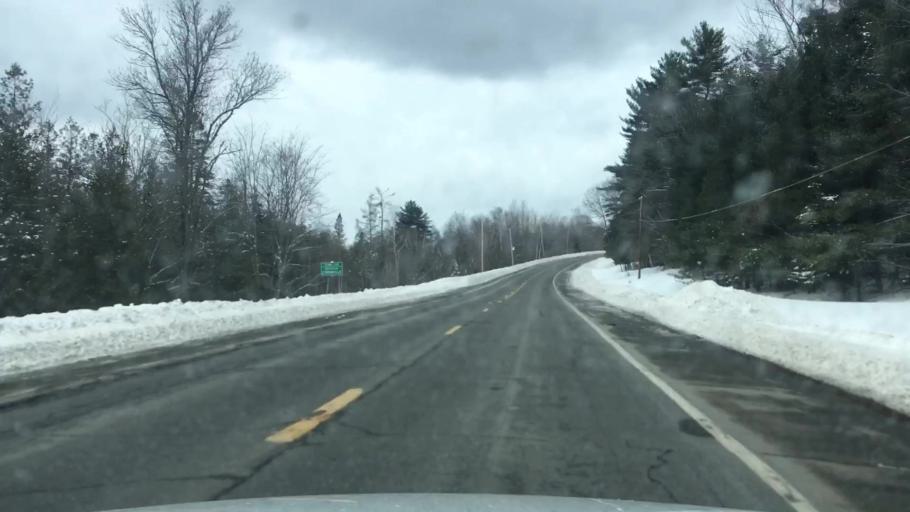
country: US
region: Maine
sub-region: Somerset County
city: Cornville
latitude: 44.8095
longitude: -69.7057
